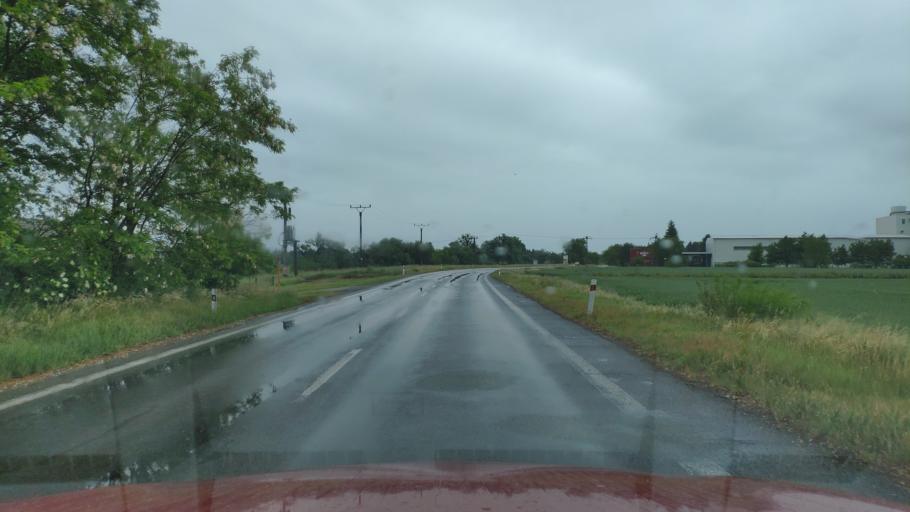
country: HU
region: Borsod-Abauj-Zemplen
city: Karcsa
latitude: 48.3932
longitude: 21.7987
